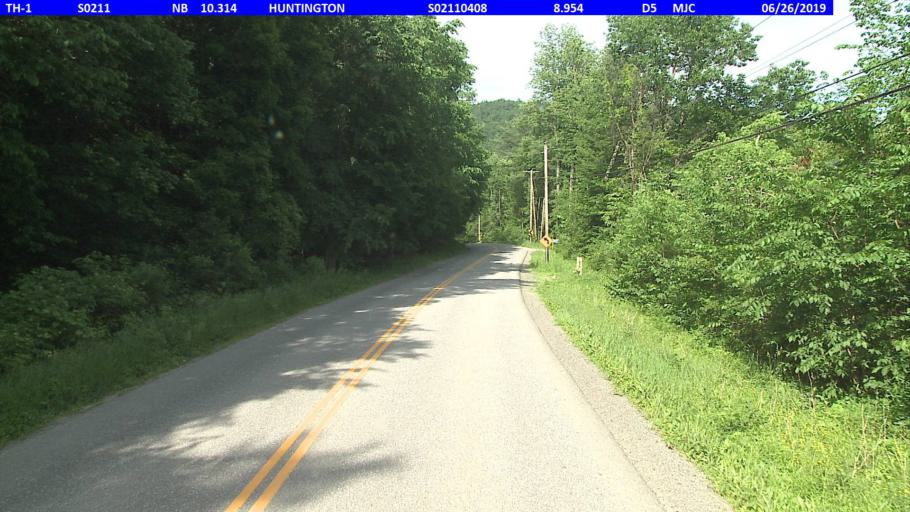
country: US
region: Vermont
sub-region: Chittenden County
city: Hinesburg
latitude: 44.3430
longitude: -72.9954
